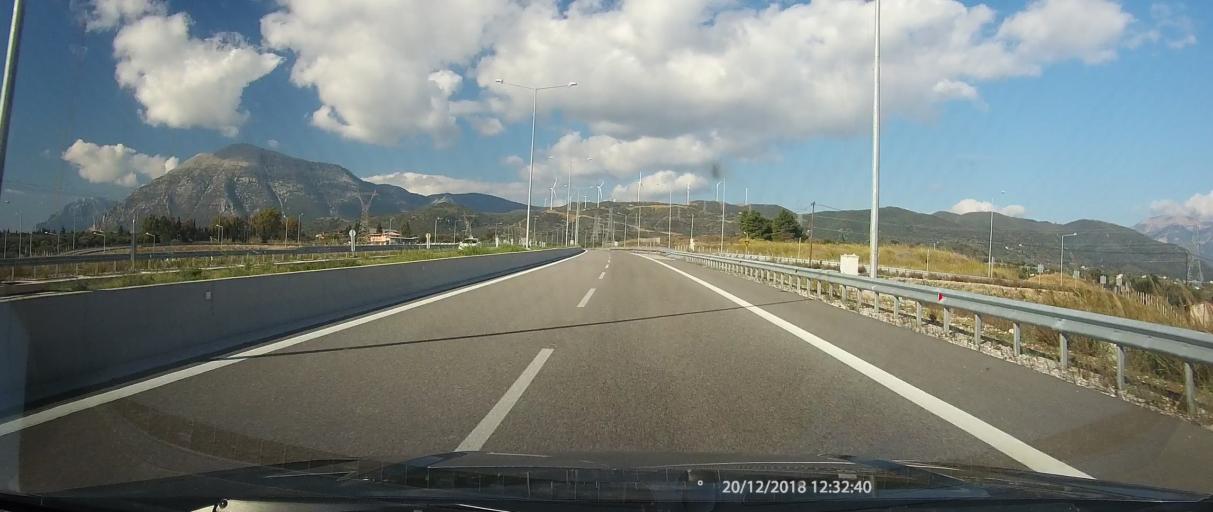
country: GR
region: West Greece
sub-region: Nomos Aitolias kai Akarnanias
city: Antirrio
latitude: 38.3418
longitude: 21.7604
